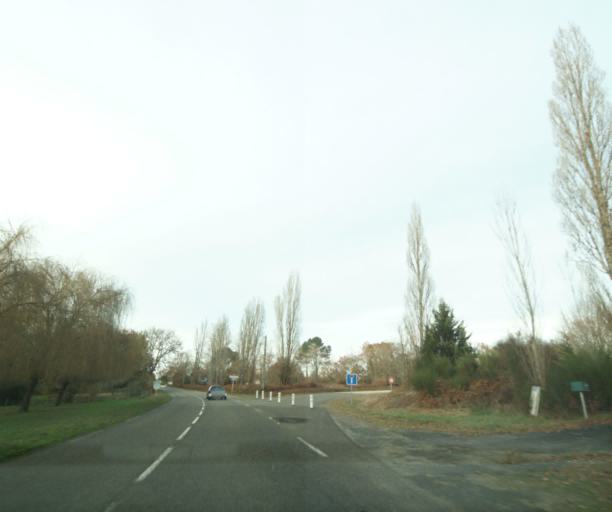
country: FR
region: Aquitaine
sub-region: Departement de la Gironde
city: Prechac
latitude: 44.2850
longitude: -0.2544
